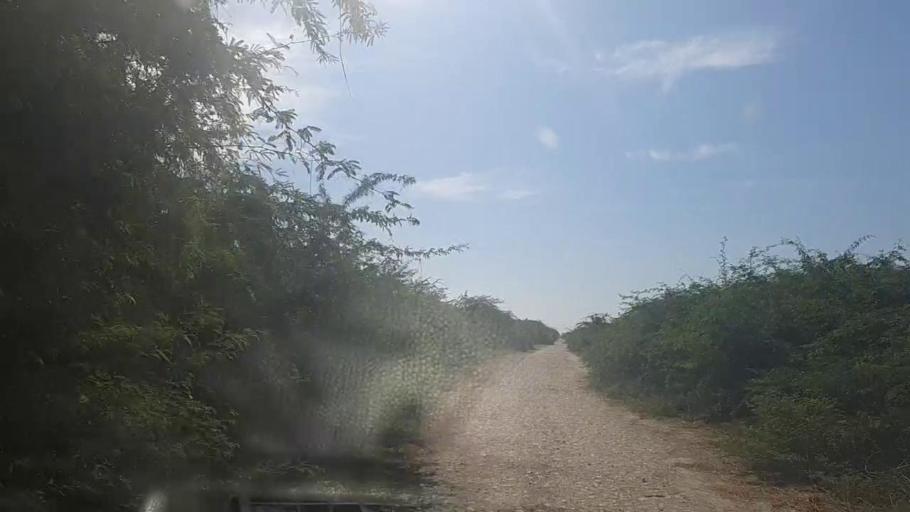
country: PK
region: Sindh
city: Mirpur Batoro
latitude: 24.6776
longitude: 68.1825
